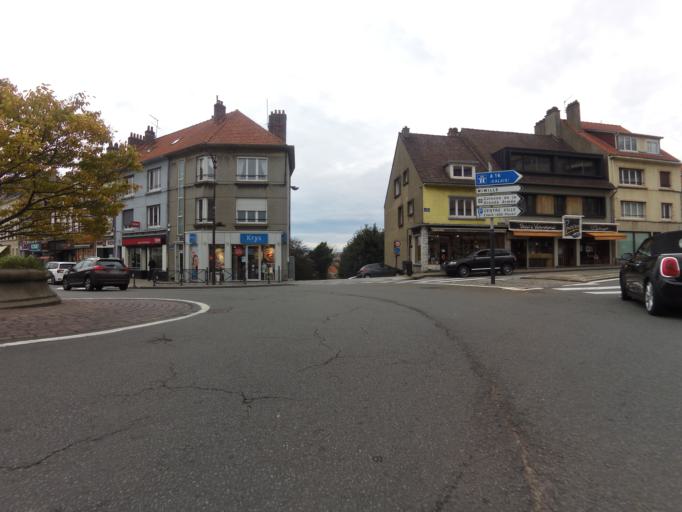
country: FR
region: Nord-Pas-de-Calais
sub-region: Departement du Pas-de-Calais
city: Saint-Martin-Boulogne
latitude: 50.7276
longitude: 1.6184
